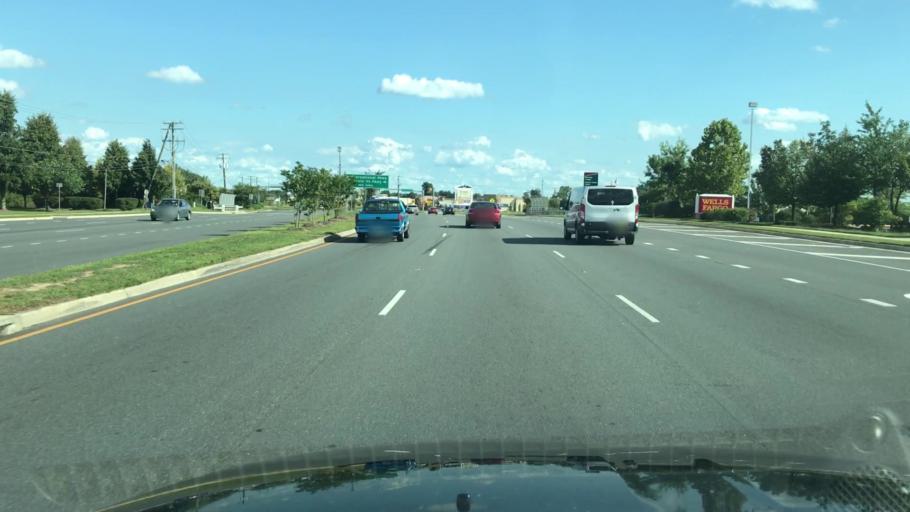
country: US
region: Virginia
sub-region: Stafford County
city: Falmouth
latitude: 38.3604
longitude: -77.5197
